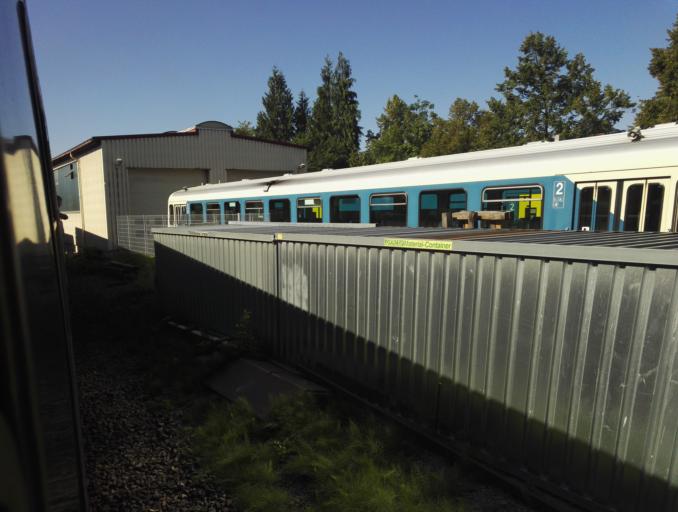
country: DE
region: Baden-Wuerttemberg
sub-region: Regierungsbezirk Stuttgart
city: Rudersberg
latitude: 48.8836
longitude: 9.5310
